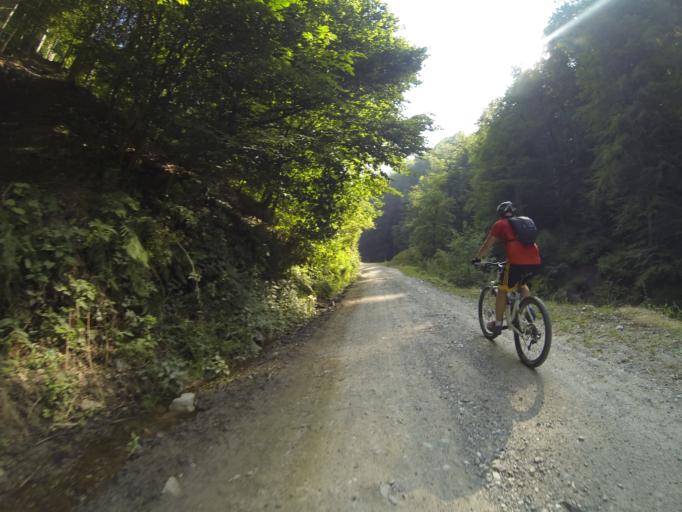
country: RO
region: Valcea
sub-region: Comuna Costesti
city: Bistrita
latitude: 45.2113
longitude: 24.0020
